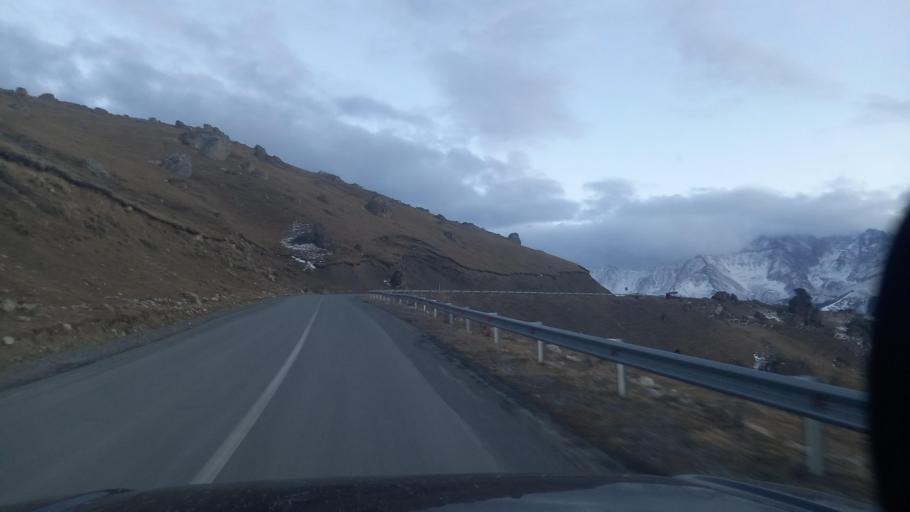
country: RU
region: Ingushetiya
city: Dzhayrakh
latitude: 42.8222
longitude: 44.8293
